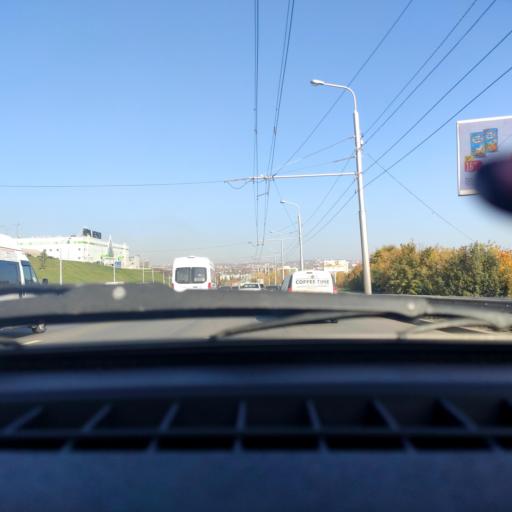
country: RU
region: Bashkortostan
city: Ufa
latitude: 54.7569
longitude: 56.0386
